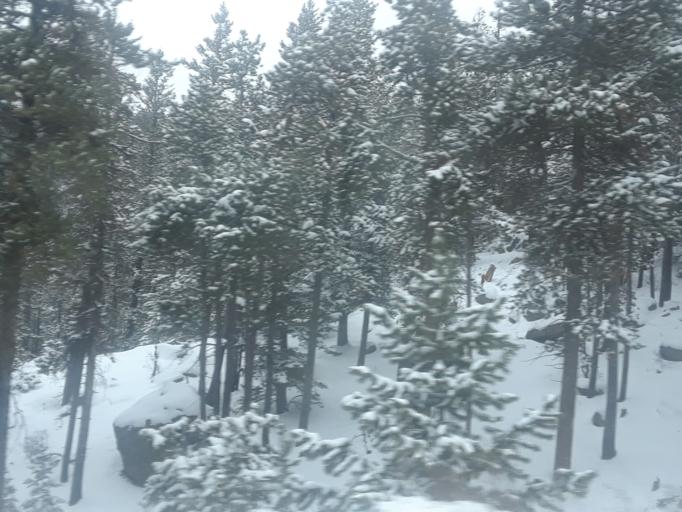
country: US
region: Colorado
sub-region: Boulder County
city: Coal Creek
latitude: 39.9307
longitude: -105.4225
